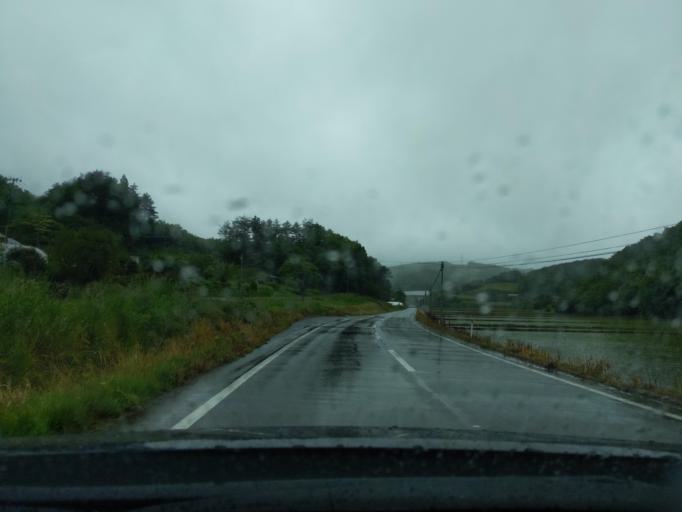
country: JP
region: Fukushima
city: Funehikimachi-funehiki
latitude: 37.6046
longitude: 140.6471
